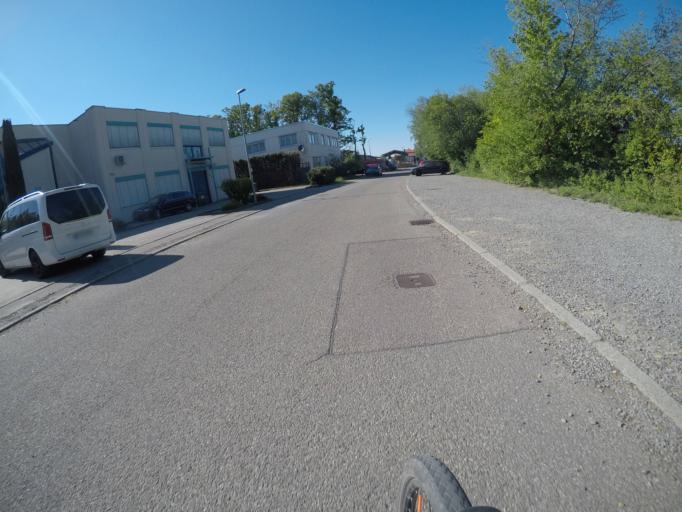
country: DE
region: Baden-Wuerttemberg
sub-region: Karlsruhe Region
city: Wimsheim
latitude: 48.8442
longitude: 8.8284
